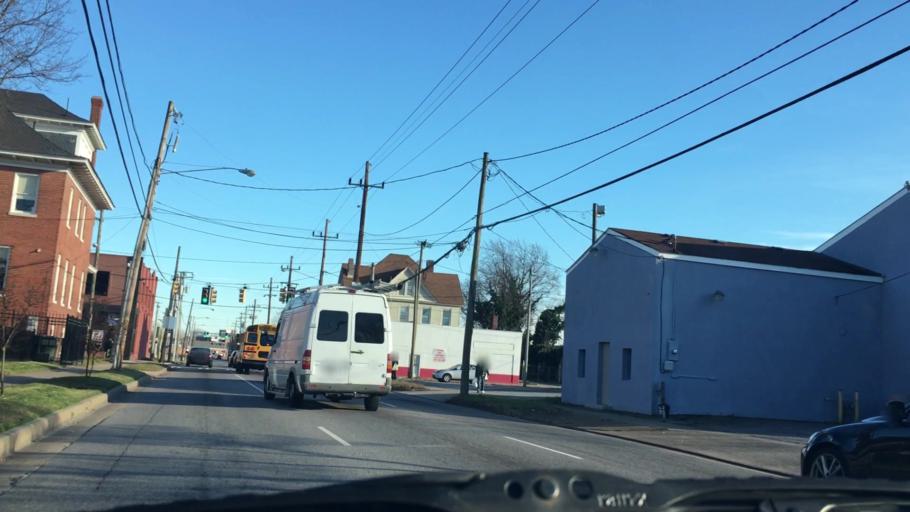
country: US
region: Virginia
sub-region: City of Norfolk
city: Norfolk
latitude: 36.8713
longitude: -76.2843
